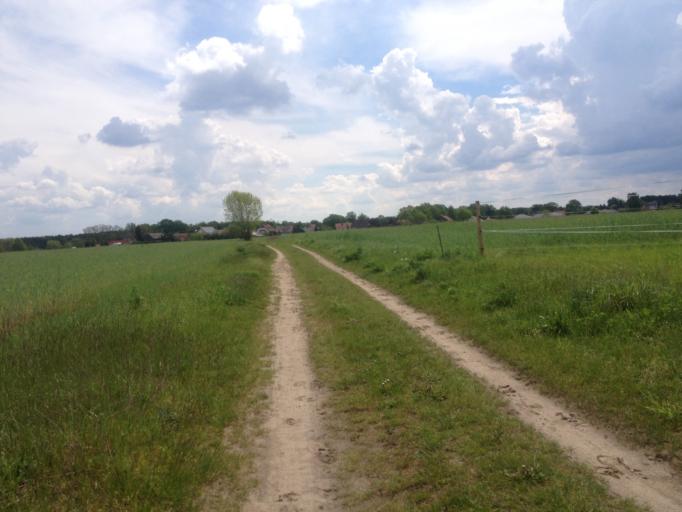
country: DE
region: Brandenburg
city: Drehnow
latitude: 51.8124
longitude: 14.3499
